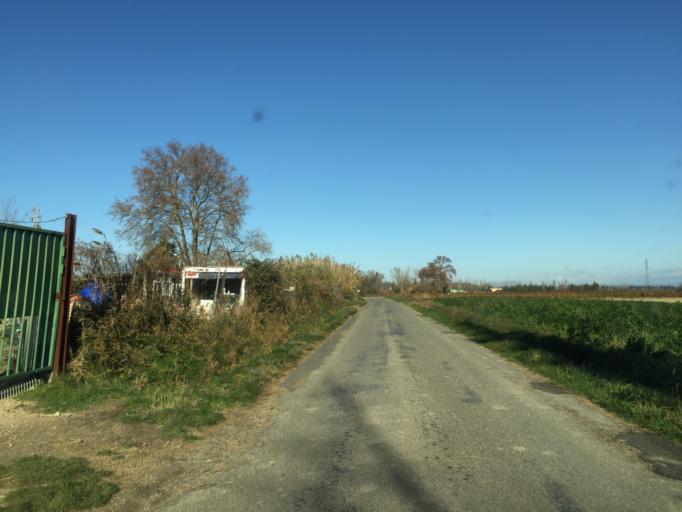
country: FR
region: Provence-Alpes-Cote d'Azur
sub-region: Departement du Vaucluse
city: Bedarrides
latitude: 44.0514
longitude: 4.8986
